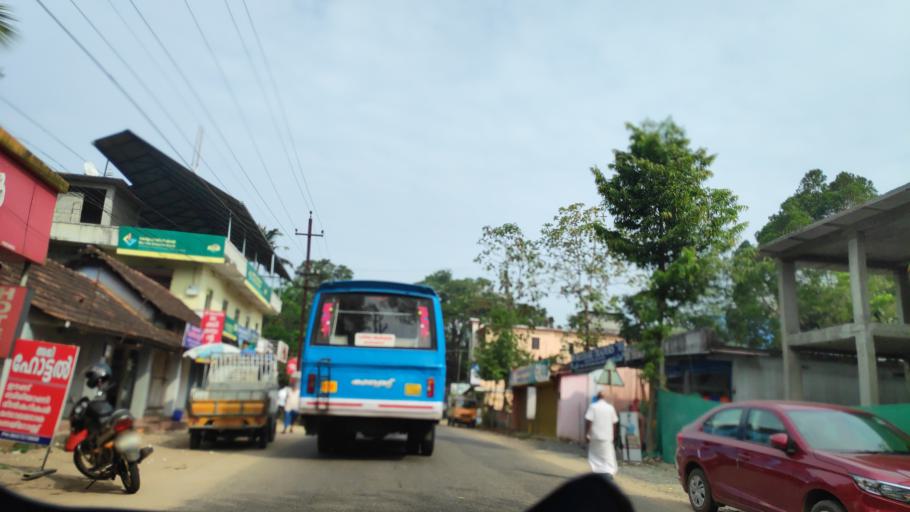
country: IN
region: Kerala
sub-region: Alappuzha
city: Kutiatodu
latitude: 9.8013
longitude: 76.3537
